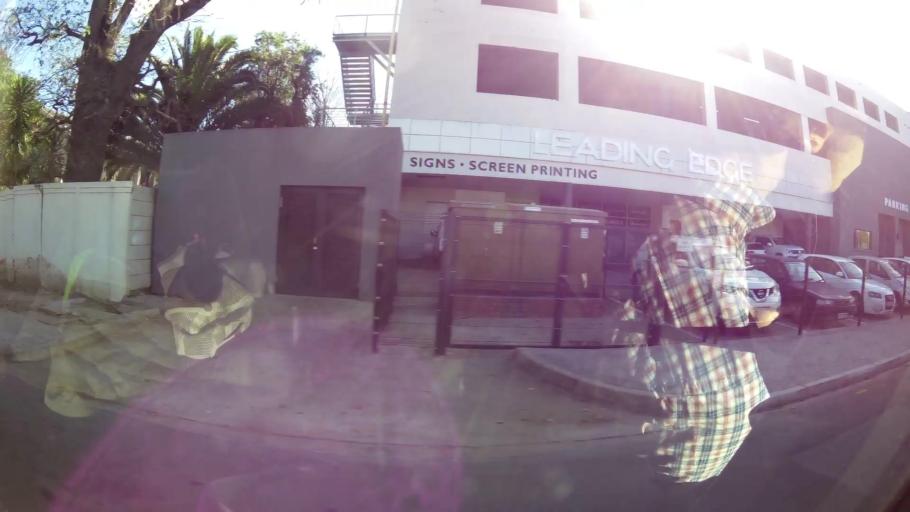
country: ZA
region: Western Cape
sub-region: Eden District Municipality
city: George
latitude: -33.9575
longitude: 22.4617
